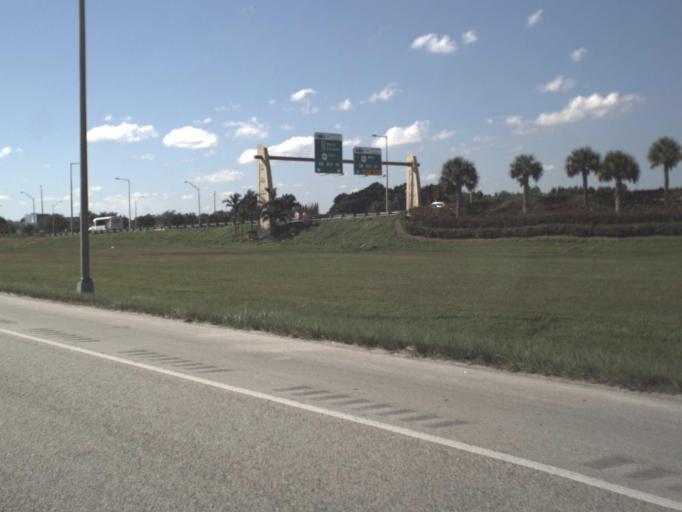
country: US
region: Florida
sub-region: Miami-Dade County
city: Sweetwater
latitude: 25.7742
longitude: -80.3861
